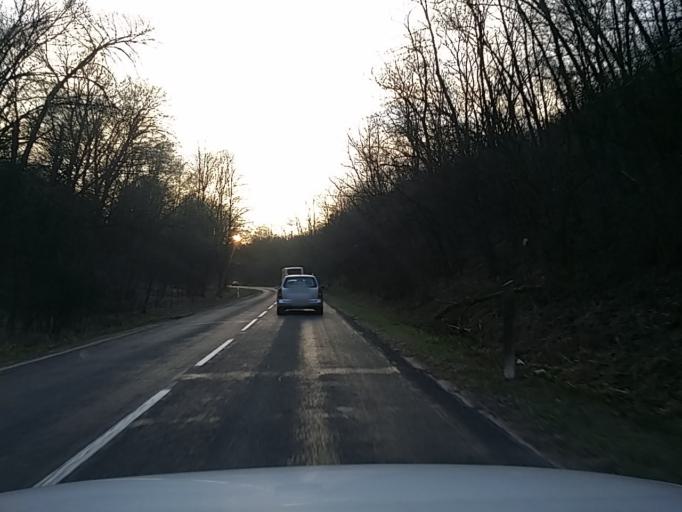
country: HU
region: Nograd
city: Matranovak
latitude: 48.0130
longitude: 20.0343
